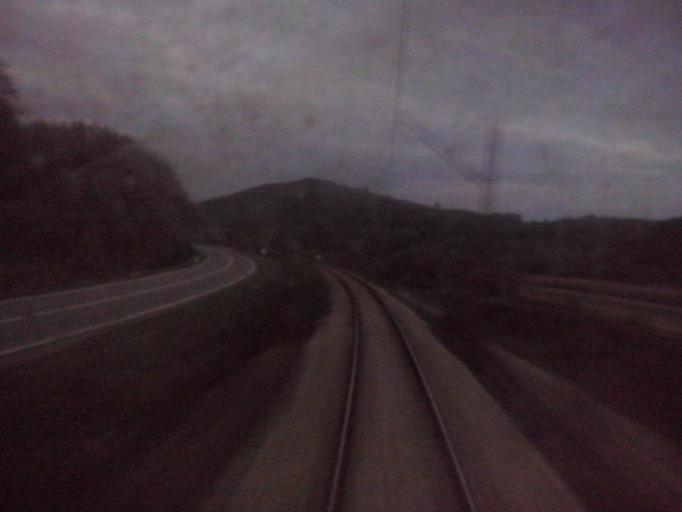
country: RS
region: Central Serbia
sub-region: Kolubarski Okrug
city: Mionica
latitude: 44.3161
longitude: 20.0678
